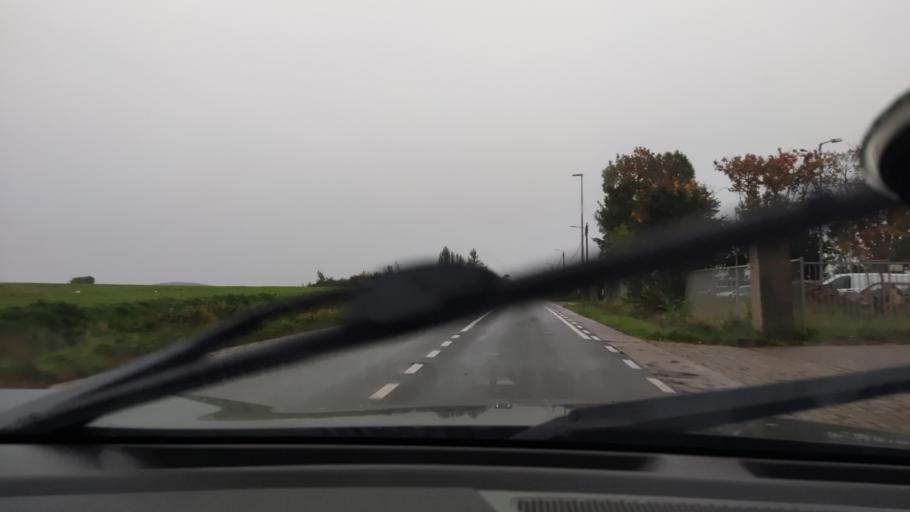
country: BE
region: Wallonia
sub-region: Province du Brabant Wallon
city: Jodoigne
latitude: 50.7144
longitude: 4.8936
